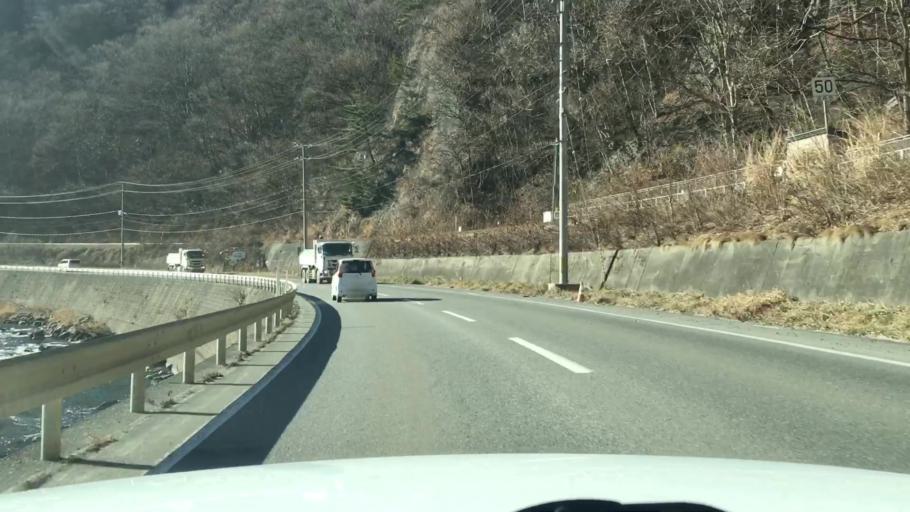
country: JP
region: Iwate
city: Miyako
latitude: 39.6109
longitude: 141.7756
